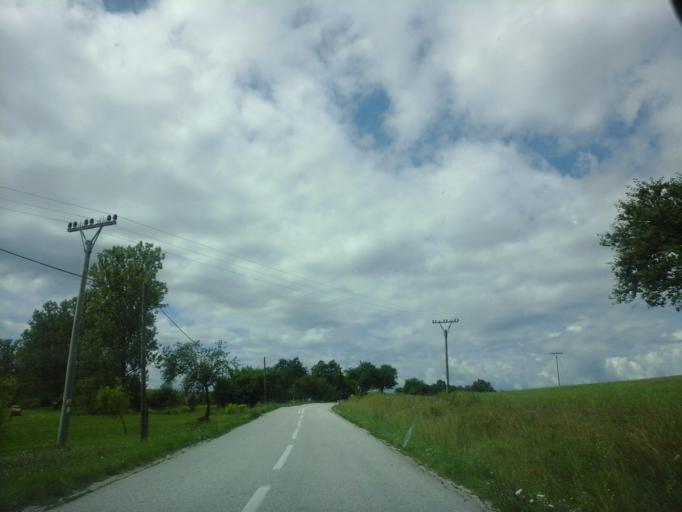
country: HU
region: Borsod-Abauj-Zemplen
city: Putnok
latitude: 48.4778
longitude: 20.4664
